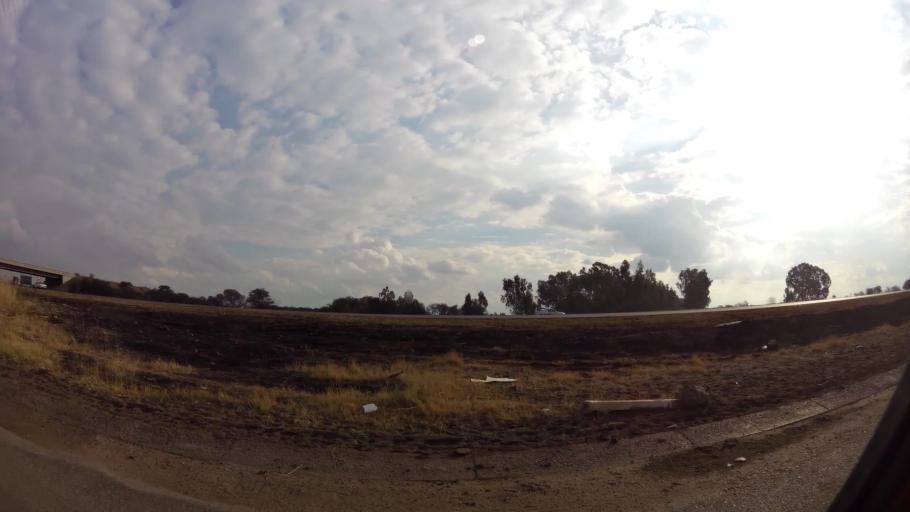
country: ZA
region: Gauteng
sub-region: Sedibeng District Municipality
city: Vereeniging
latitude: -26.6839
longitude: 27.9056
